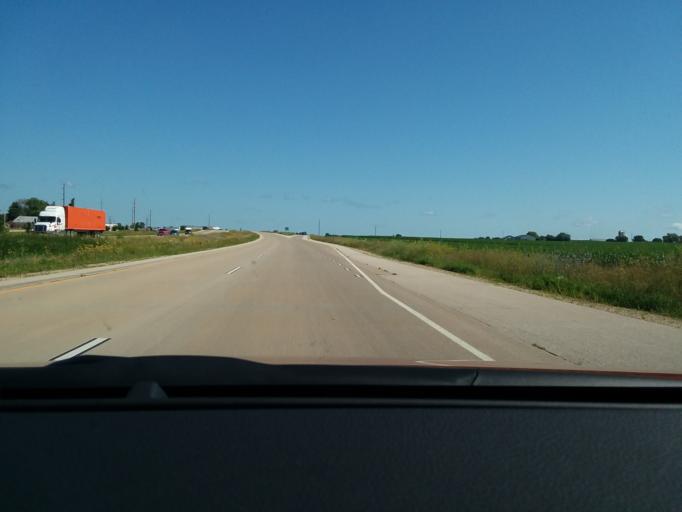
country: US
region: Wisconsin
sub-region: Dane County
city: De Forest
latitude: 43.2454
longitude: -89.3227
